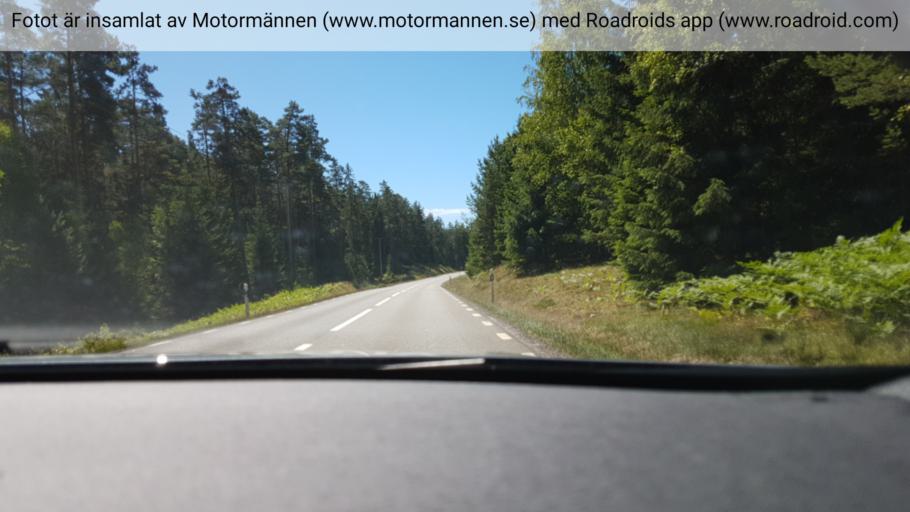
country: SE
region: Joenkoeping
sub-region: Mullsjo Kommun
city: Mullsjoe
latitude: 57.7873
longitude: 13.8356
